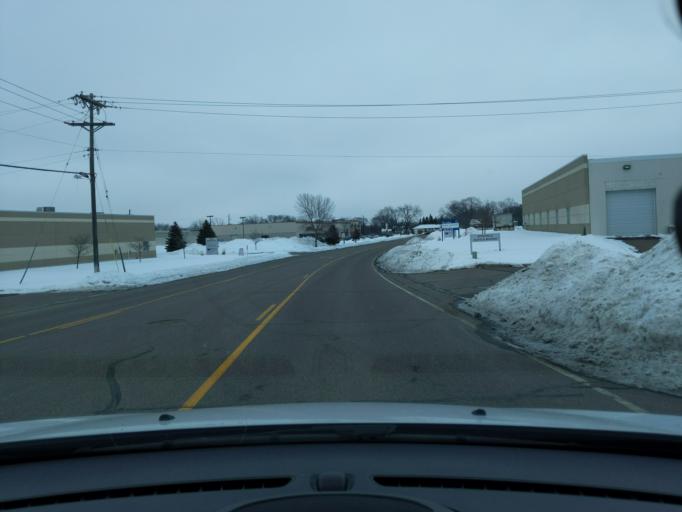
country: US
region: Minnesota
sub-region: Ramsey County
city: Roseville
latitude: 45.0179
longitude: -93.1810
